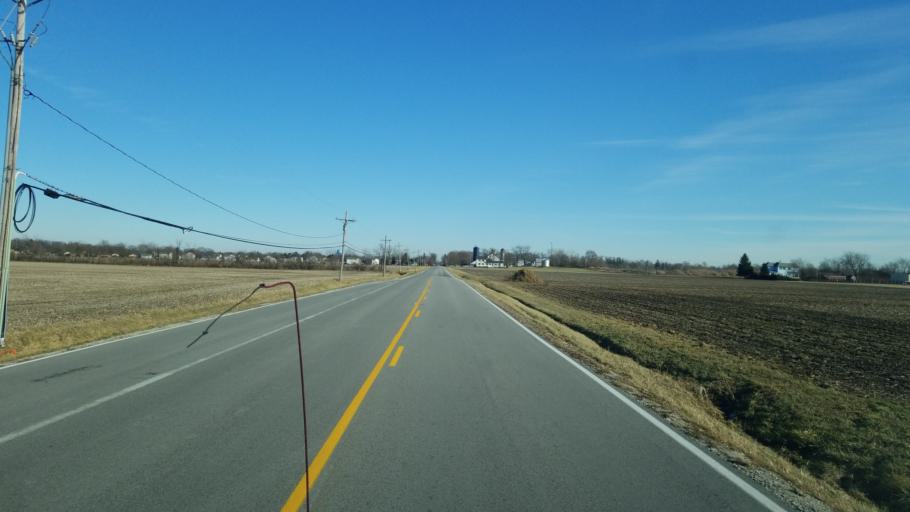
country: US
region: Ohio
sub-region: Sandusky County
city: Stony Prairie
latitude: 41.3493
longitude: -83.1584
